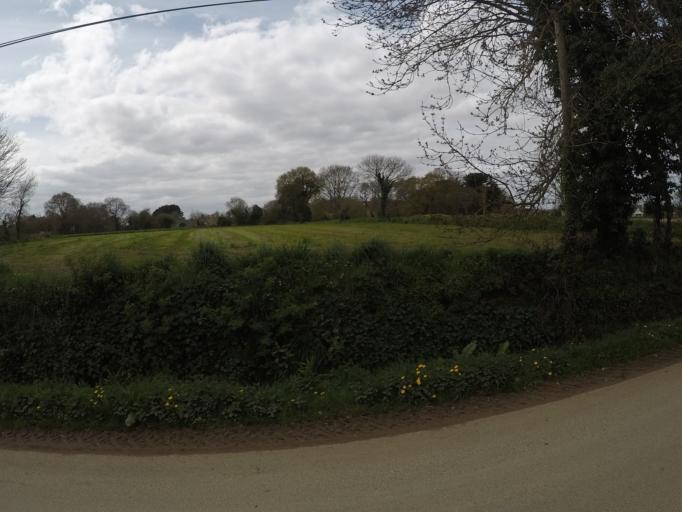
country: FR
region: Brittany
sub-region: Departement des Cotes-d'Armor
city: Plouha
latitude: 48.7112
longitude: -2.9548
